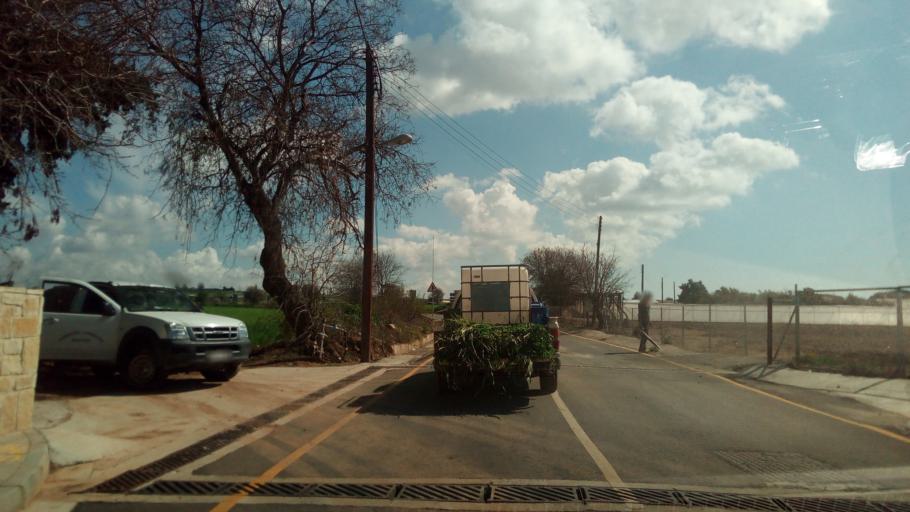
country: CY
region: Pafos
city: Mesogi
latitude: 34.7416
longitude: 32.5385
